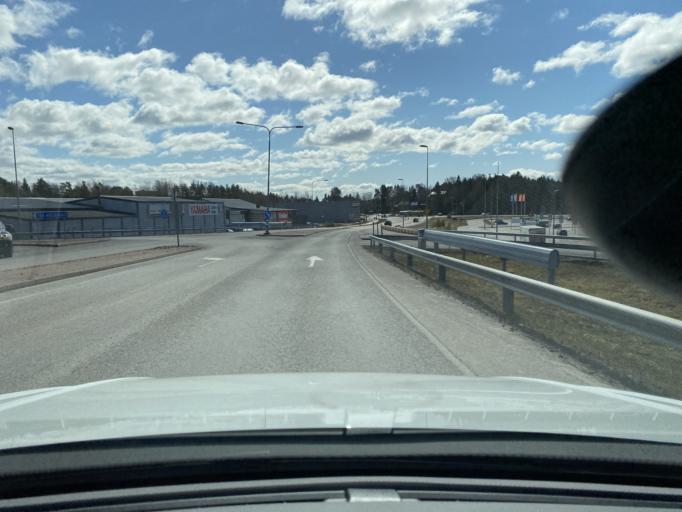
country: FI
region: Varsinais-Suomi
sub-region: Turku
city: Rusko
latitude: 60.4959
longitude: 22.2314
